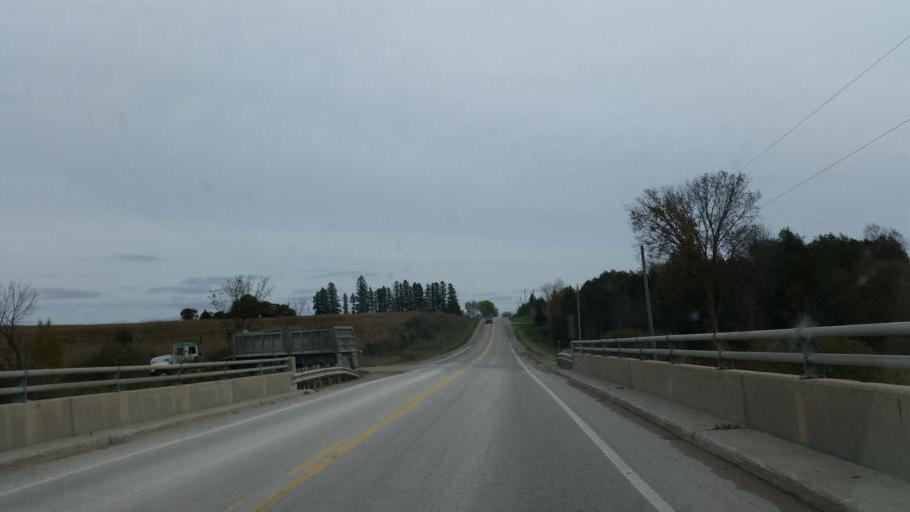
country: CA
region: Ontario
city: Wingham
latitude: 43.9937
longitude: -81.3352
